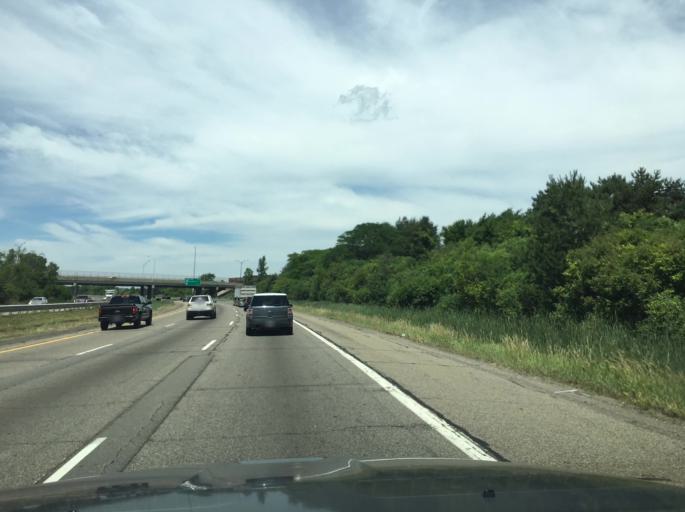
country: US
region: Michigan
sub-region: Oakland County
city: Troy
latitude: 42.6037
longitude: -83.1663
